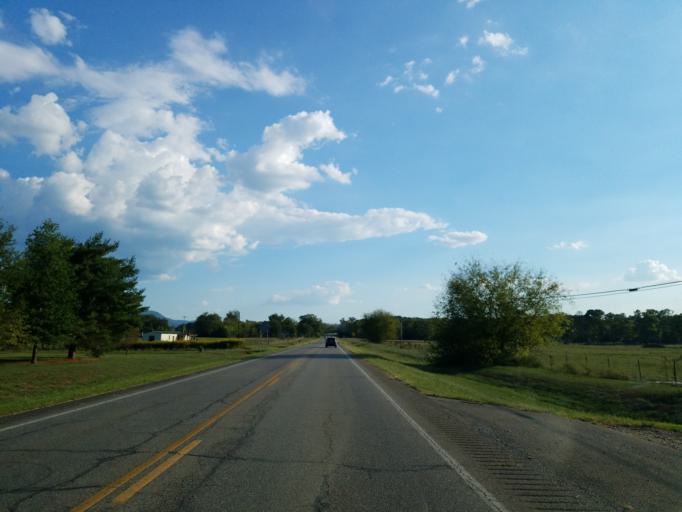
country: US
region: Georgia
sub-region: Murray County
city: Chatsworth
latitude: 34.8898
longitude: -84.7501
